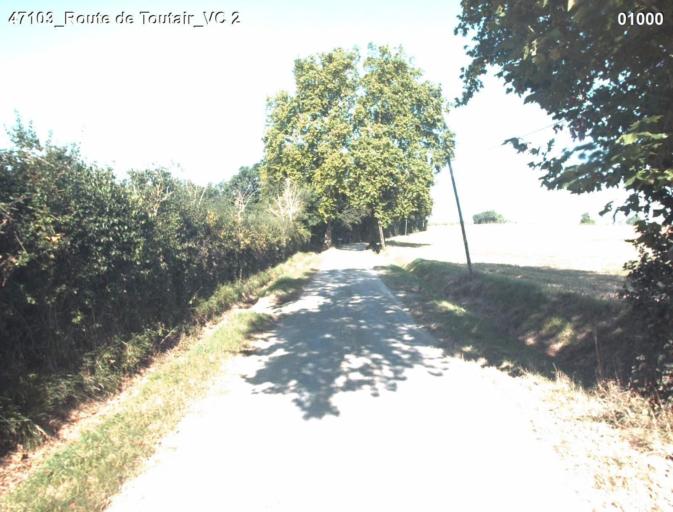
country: FR
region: Aquitaine
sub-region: Departement du Lot-et-Garonne
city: Nerac
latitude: 44.0780
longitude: 0.3259
